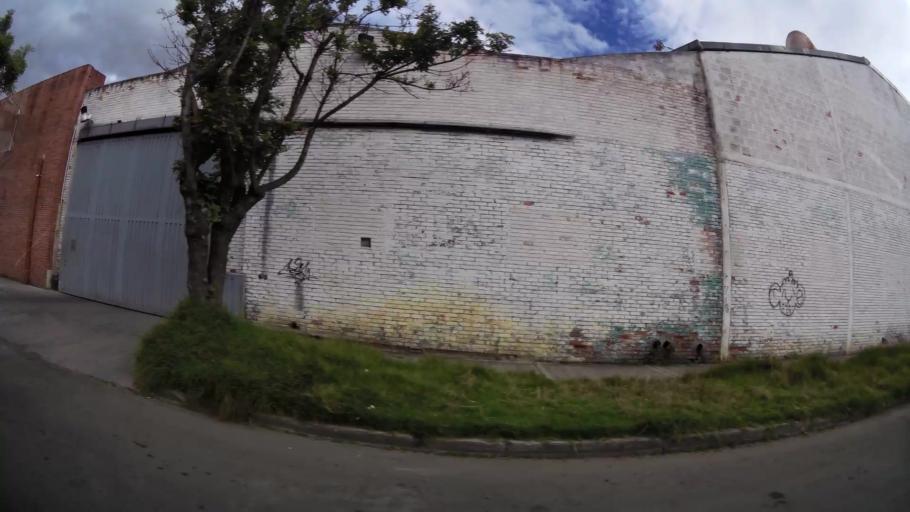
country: CO
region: Bogota D.C.
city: Bogota
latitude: 4.6216
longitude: -74.0984
